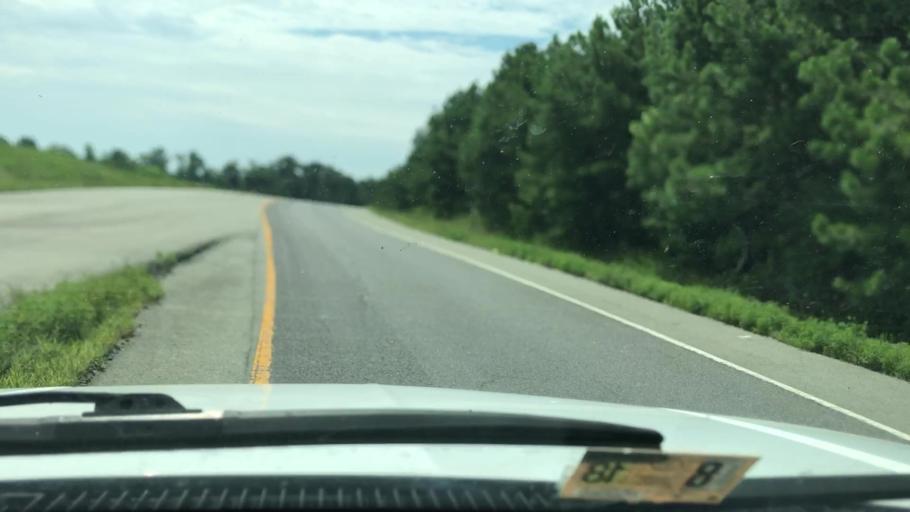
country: US
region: Virginia
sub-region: Henrico County
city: Short Pump
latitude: 37.5981
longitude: -77.6694
